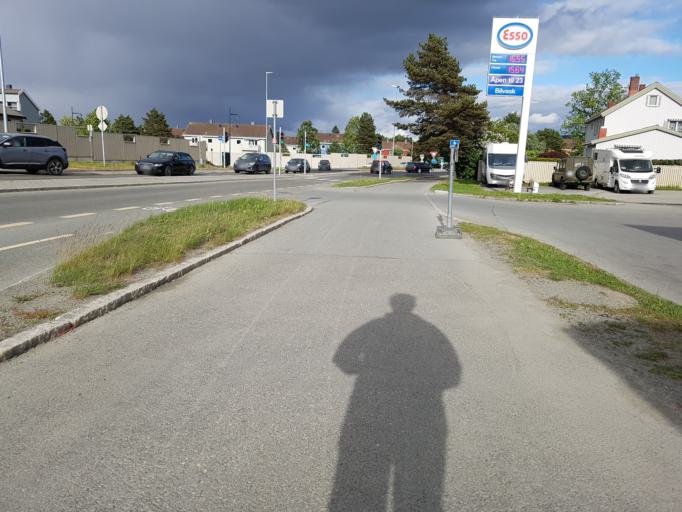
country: NO
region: Sor-Trondelag
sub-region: Trondheim
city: Trondheim
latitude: 63.4302
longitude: 10.4528
